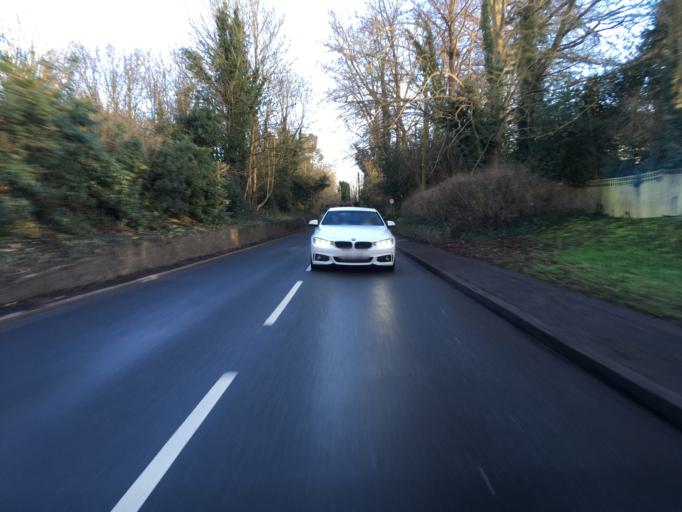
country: GB
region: England
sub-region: Warwickshire
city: Stratford-upon-Avon
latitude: 52.2433
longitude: -1.7377
